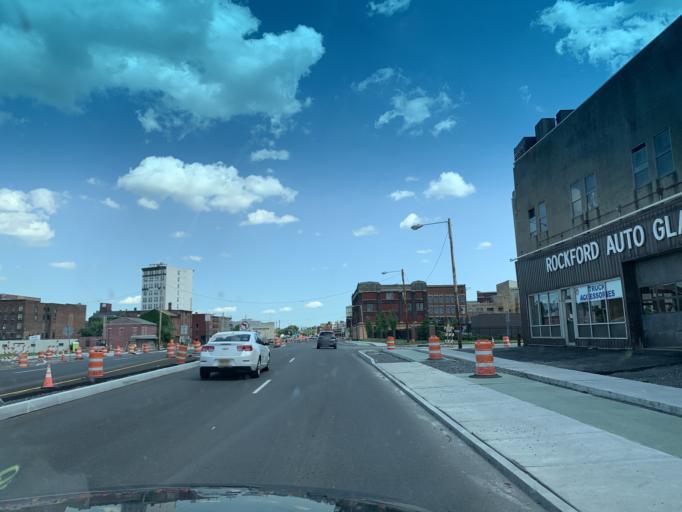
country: US
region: New York
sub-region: Oneida County
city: Utica
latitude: 43.1038
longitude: -75.2318
